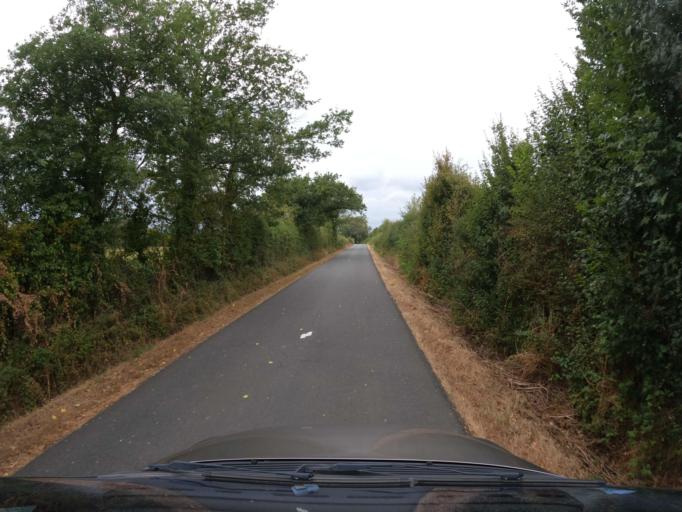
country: FR
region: Pays de la Loire
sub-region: Departement de Maine-et-Loire
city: La Romagne
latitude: 47.0445
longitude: -0.9831
